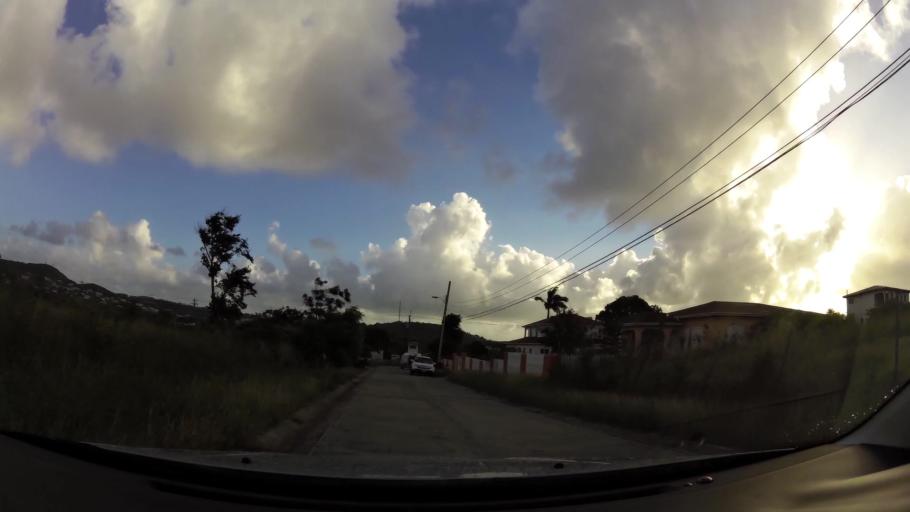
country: AG
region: Saint John
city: Saint John's
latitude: 17.1623
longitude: -61.8309
